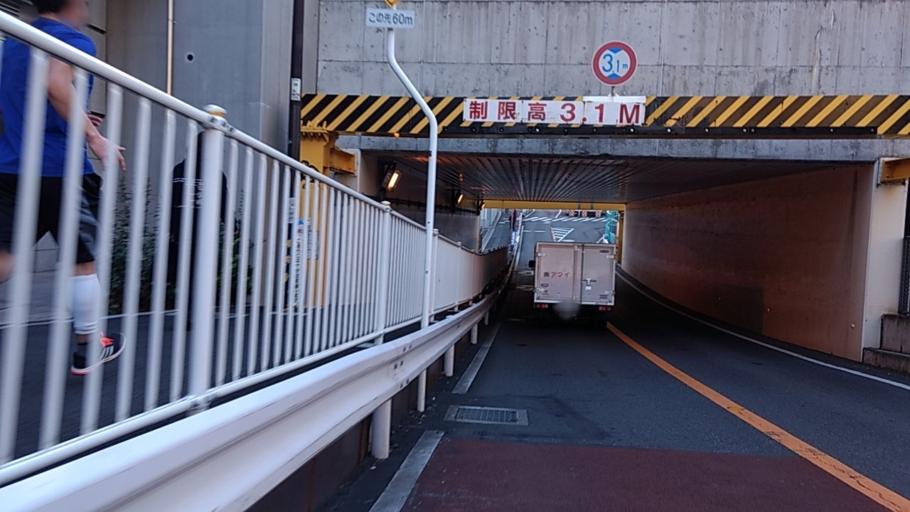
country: JP
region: Tokyo
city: Tokyo
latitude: 35.7093
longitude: 139.7029
